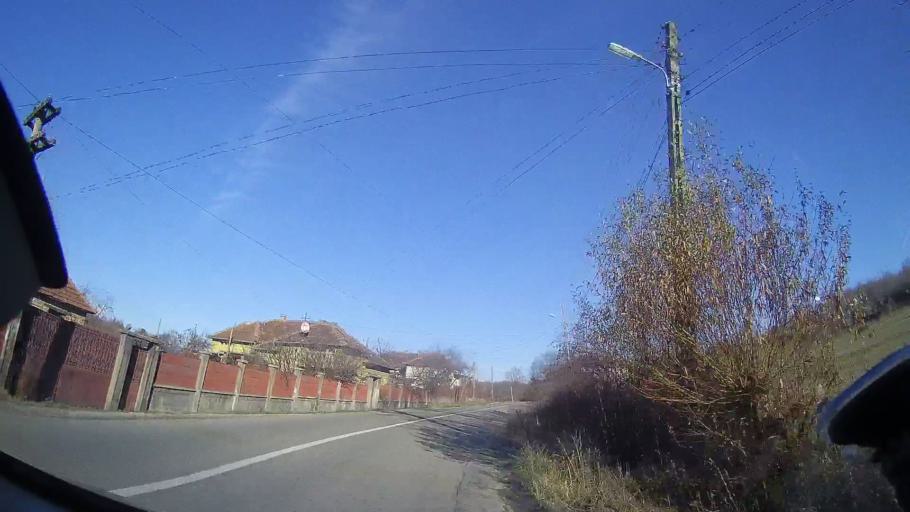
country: RO
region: Bihor
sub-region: Comuna Bratca
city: Bratca
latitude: 46.9349
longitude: 22.6034
